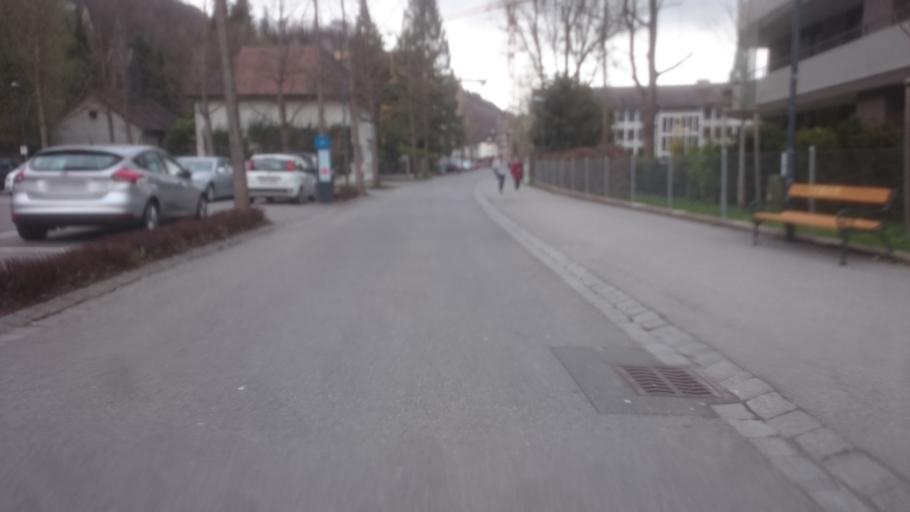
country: AT
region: Vorarlberg
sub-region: Politischer Bezirk Feldkirch
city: Feldkirch
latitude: 47.2393
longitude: 9.6020
